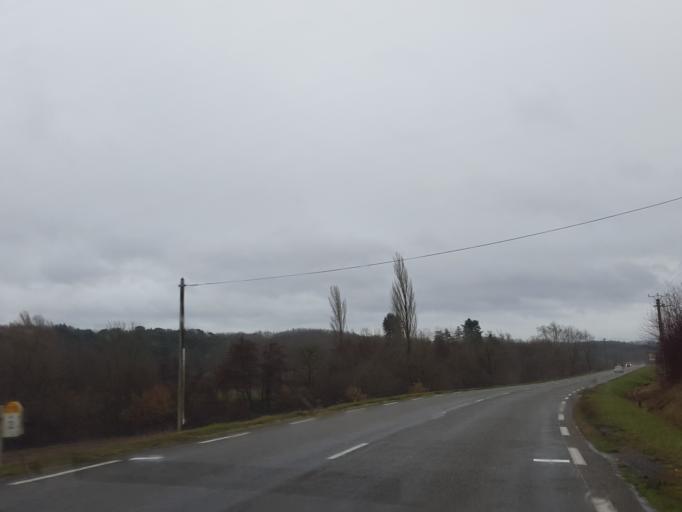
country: FR
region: Midi-Pyrenees
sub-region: Departement de l'Ariege
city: Mirepoix
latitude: 43.1091
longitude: 1.9252
